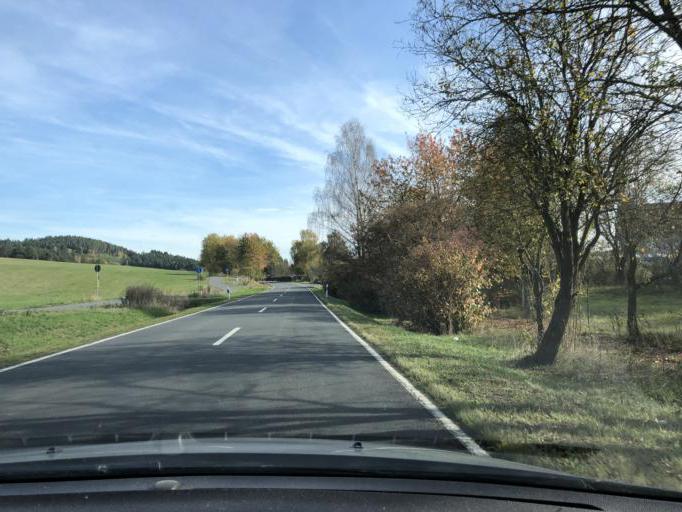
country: DE
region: Thuringia
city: Schleusingen
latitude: 50.4944
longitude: 10.7843
